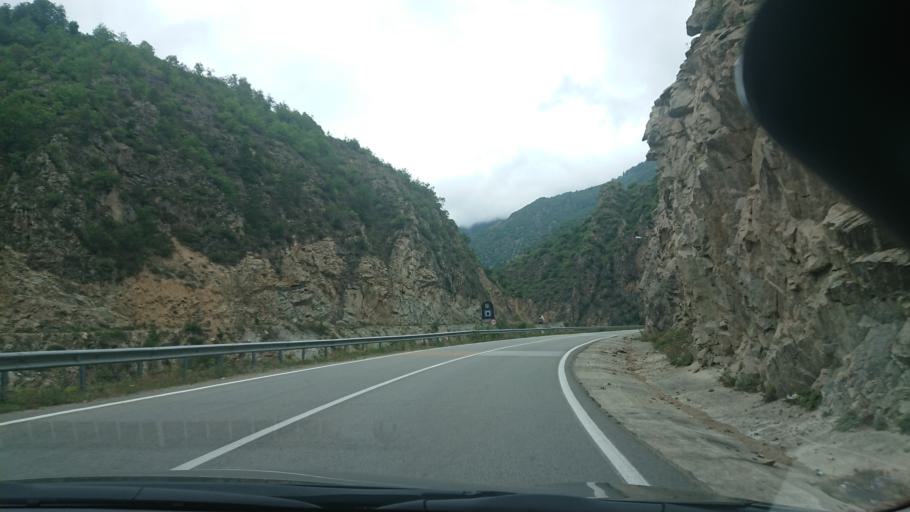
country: TR
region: Gumushane
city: Kurtun
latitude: 40.7054
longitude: 39.0663
